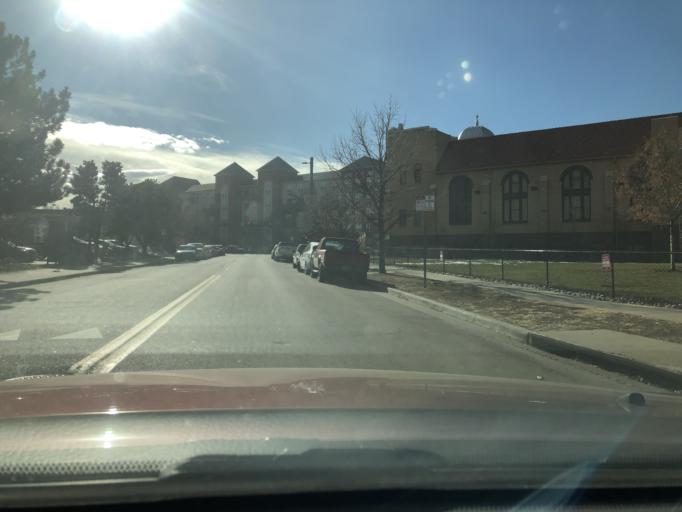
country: US
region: Colorado
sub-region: Denver County
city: Denver
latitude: 39.7486
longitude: -104.9781
